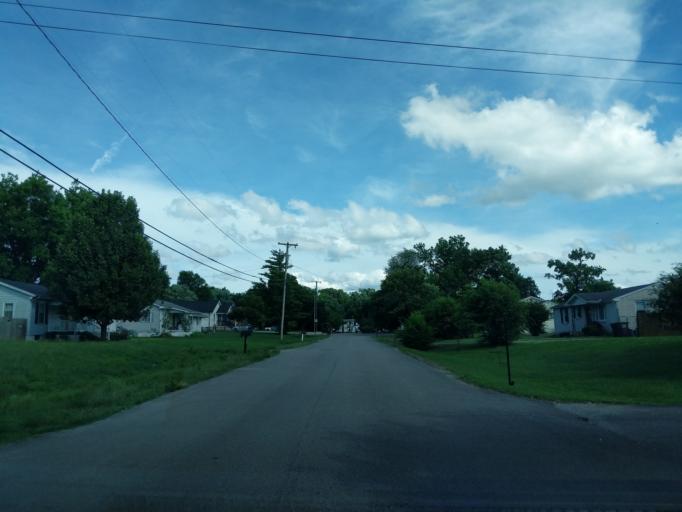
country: US
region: Tennessee
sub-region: Davidson County
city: Lakewood
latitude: 36.2733
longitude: -86.6684
